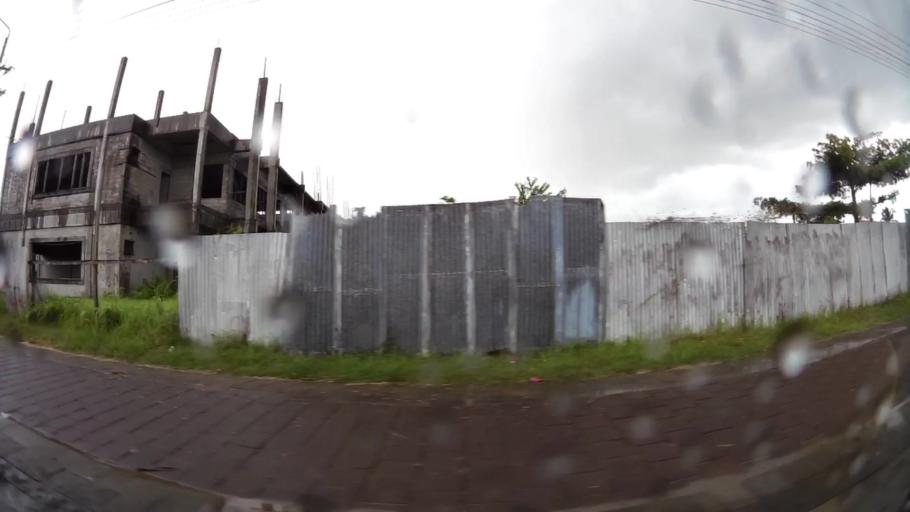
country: SR
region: Paramaribo
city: Paramaribo
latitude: 5.8221
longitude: -55.1729
